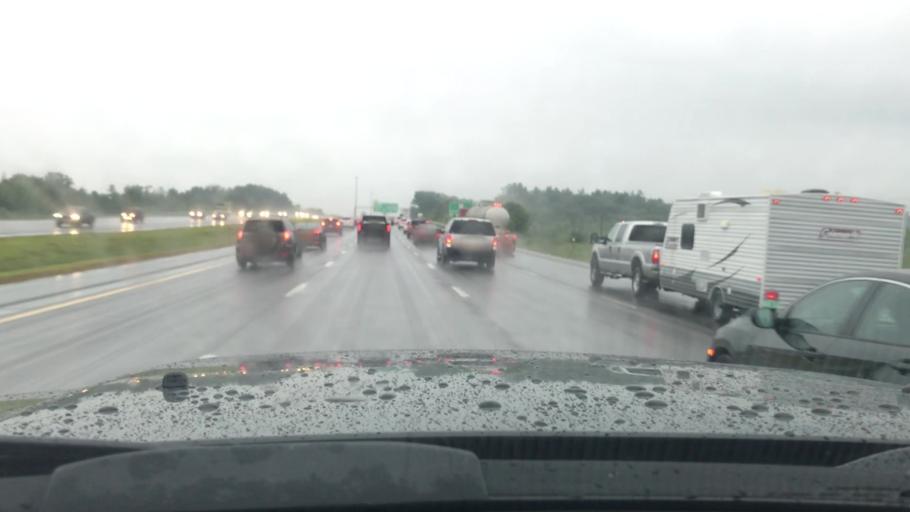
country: US
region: New Hampshire
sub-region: Rockingham County
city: Greenland
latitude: 43.0469
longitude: -70.8137
